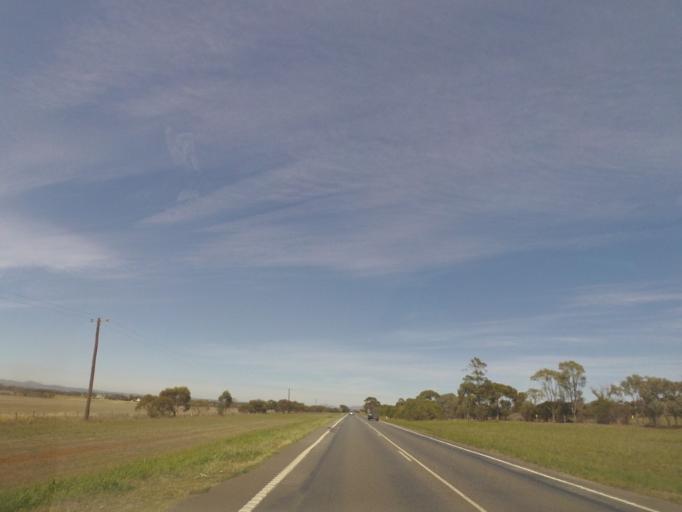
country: AU
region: Victoria
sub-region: Moorabool
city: Bacchus Marsh
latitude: -37.7787
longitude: 144.4339
